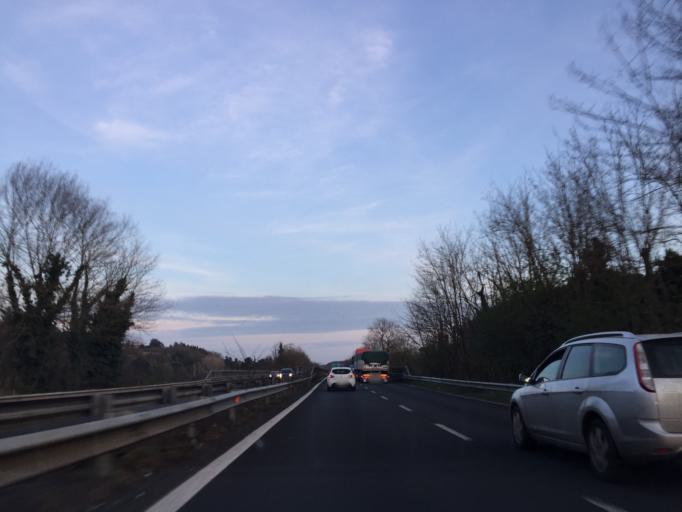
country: IT
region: Latium
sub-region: Citta metropolitana di Roma Capitale
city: Monte Caminetto
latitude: 42.0027
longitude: 12.4464
